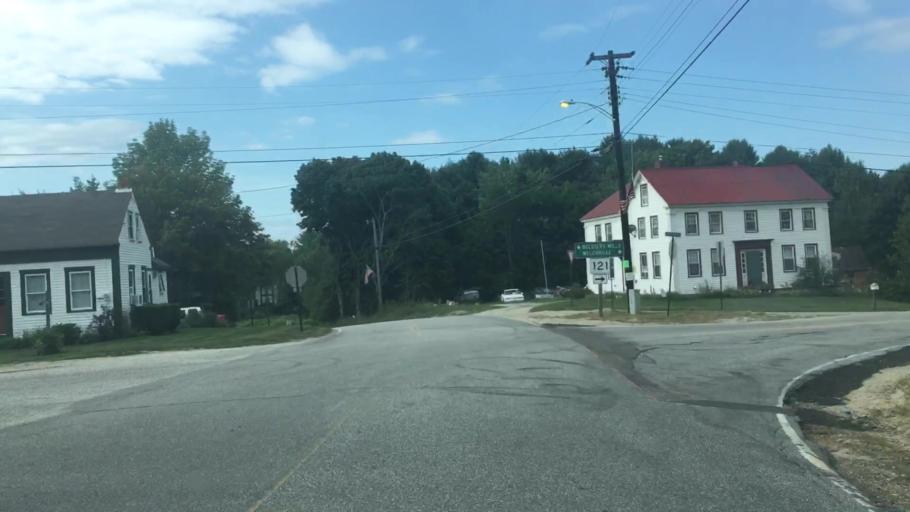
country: US
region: Maine
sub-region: Oxford County
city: Oxford
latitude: 44.0567
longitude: -70.5556
